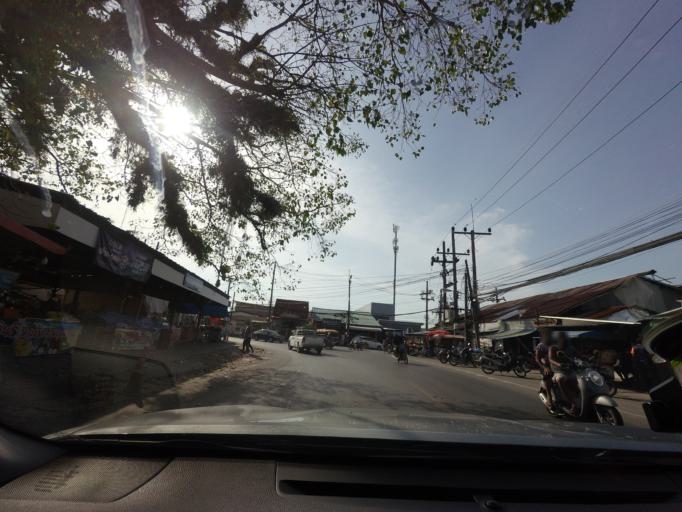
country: TH
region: Phuket
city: Thalang
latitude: 8.0166
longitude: 98.3205
